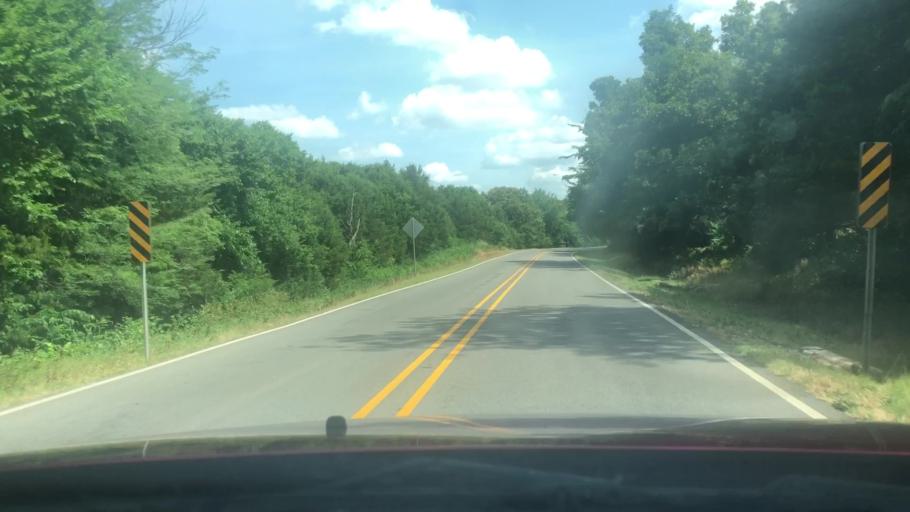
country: US
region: Arkansas
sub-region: Carroll County
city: Berryville
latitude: 36.4016
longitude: -93.5474
